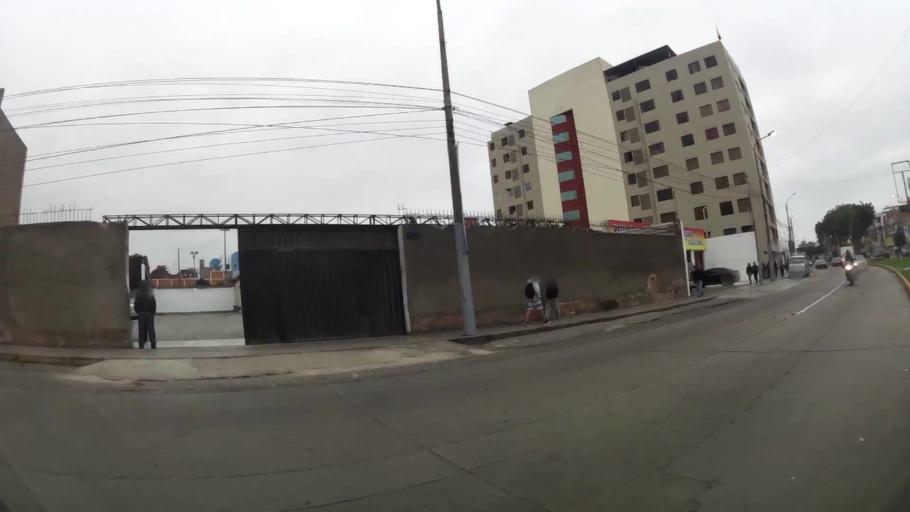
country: PE
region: Callao
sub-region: Callao
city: Callao
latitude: -12.0789
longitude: -77.0815
